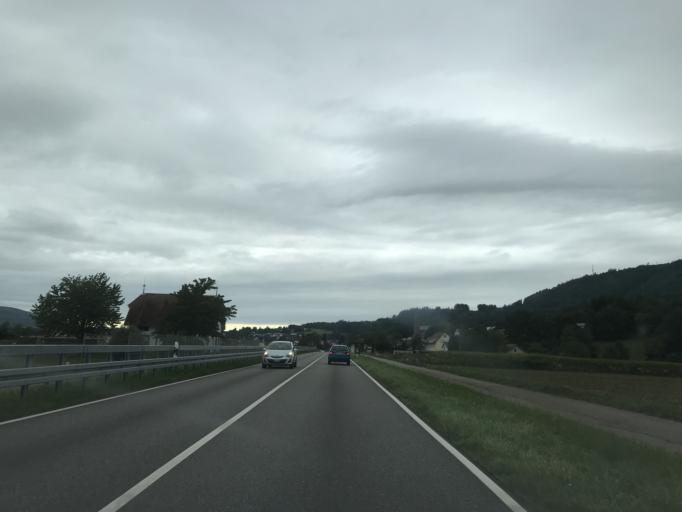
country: CH
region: Aargau
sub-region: Bezirk Laufenburg
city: Eiken
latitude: 47.5593
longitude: 7.9787
